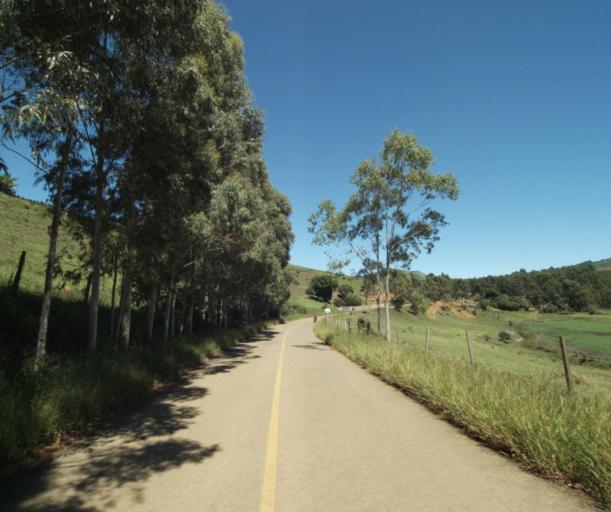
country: BR
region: Minas Gerais
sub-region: Espera Feliz
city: Espera Feliz
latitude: -20.5777
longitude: -41.8333
